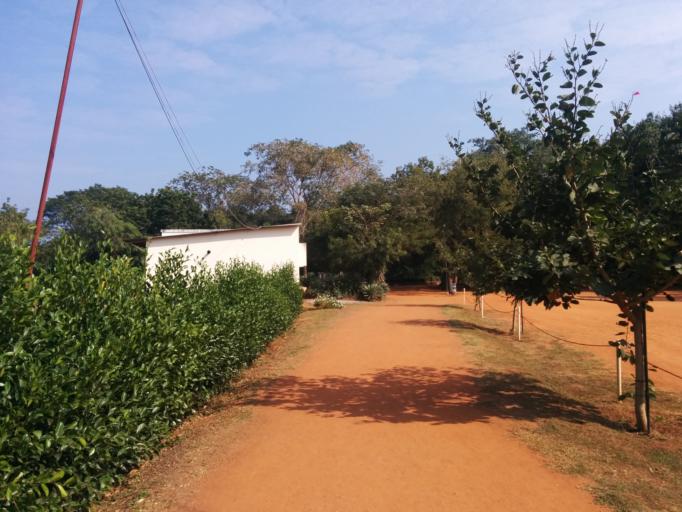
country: IN
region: Tamil Nadu
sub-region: Villupuram
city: Auroville
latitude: 12.0050
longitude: 79.8077
